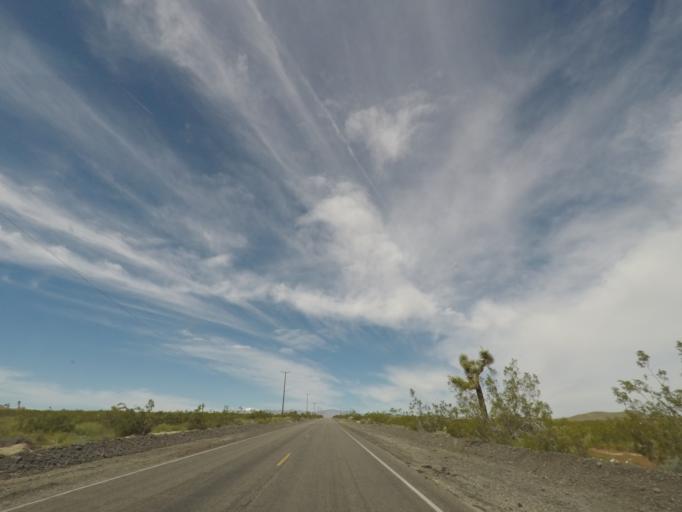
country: US
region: California
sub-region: San Bernardino County
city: Joshua Tree
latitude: 34.1930
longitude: -116.3205
